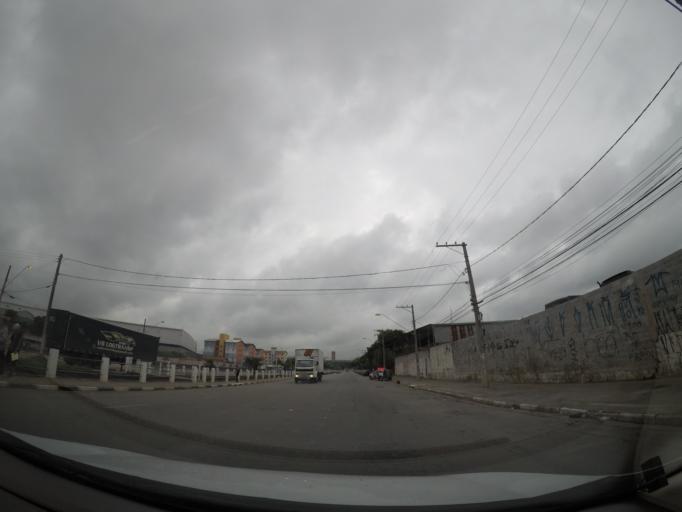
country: BR
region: Sao Paulo
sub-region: Guarulhos
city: Guarulhos
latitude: -23.4322
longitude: -46.4993
